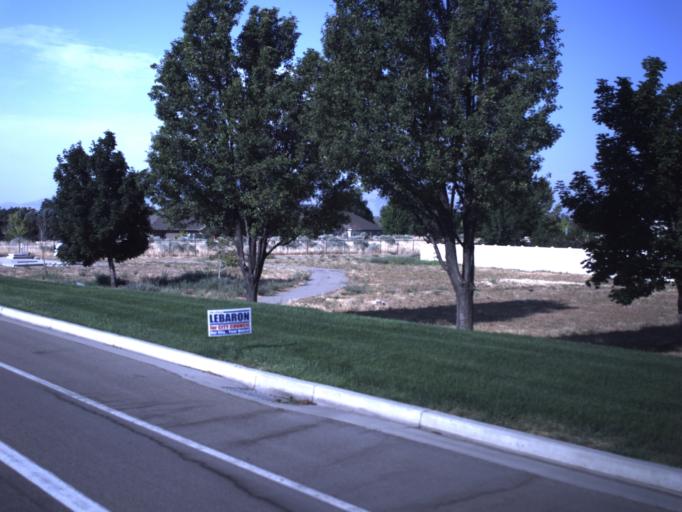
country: US
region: Utah
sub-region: Utah County
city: Cedar Hills
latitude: 40.4108
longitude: -111.7889
